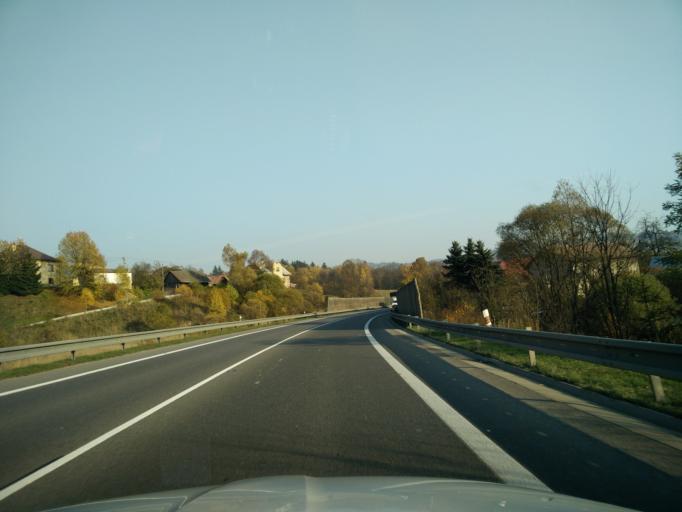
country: SK
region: Zilinsky
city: Cadca
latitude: 49.4260
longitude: 18.8318
